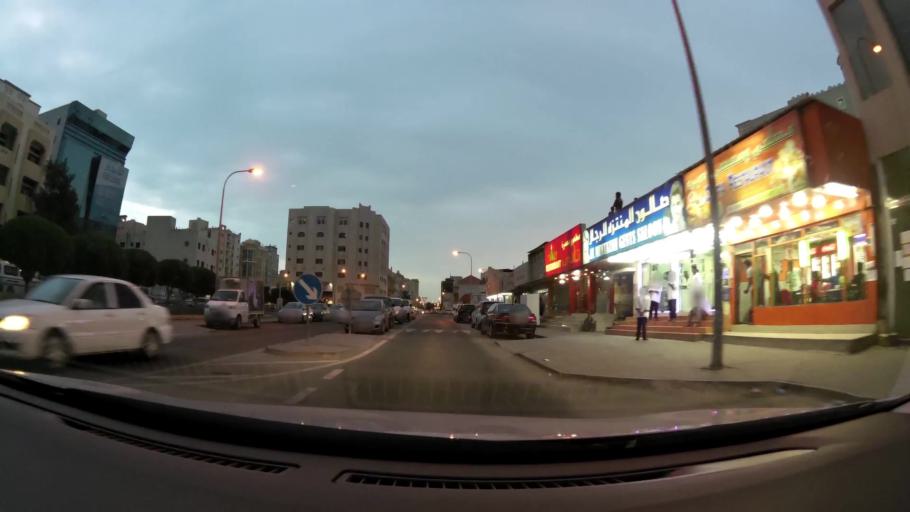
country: QA
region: Baladiyat ad Dawhah
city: Doha
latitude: 25.2730
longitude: 51.5236
